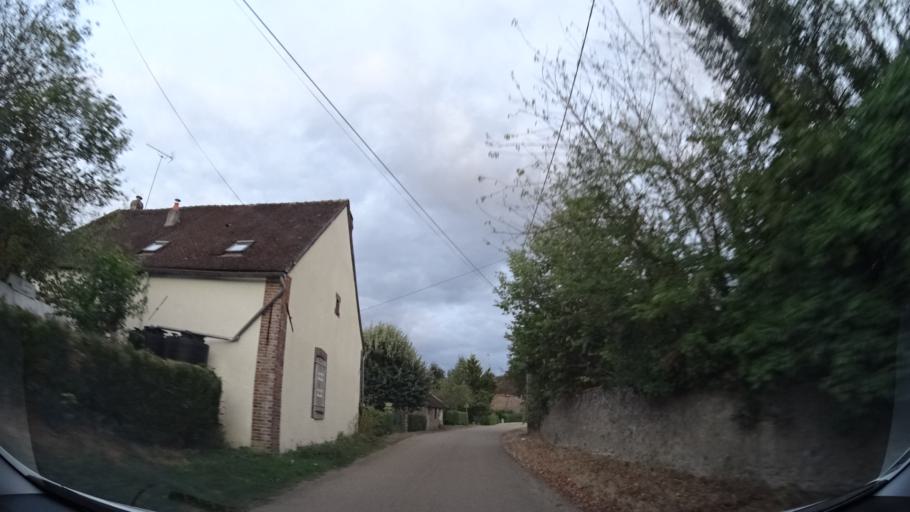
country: FR
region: Bourgogne
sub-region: Departement de l'Yonne
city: Cezy
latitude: 47.9371
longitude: 3.2764
